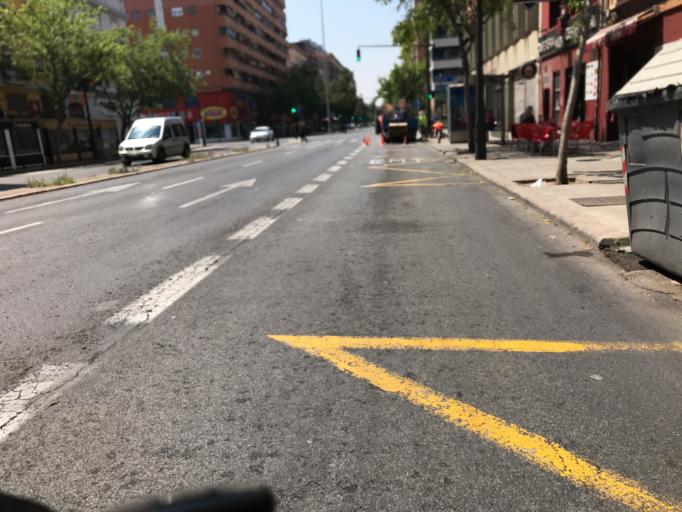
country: ES
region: Valencia
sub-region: Provincia de Valencia
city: Valencia
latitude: 39.4679
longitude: -0.3562
